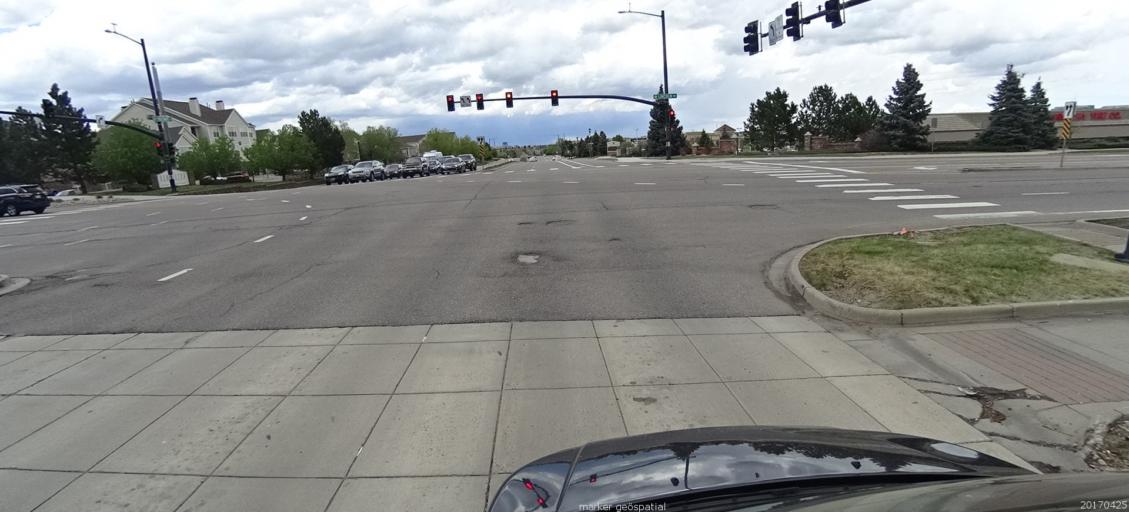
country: US
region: Colorado
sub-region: Adams County
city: Lone Tree
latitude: 39.5361
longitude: -104.8855
